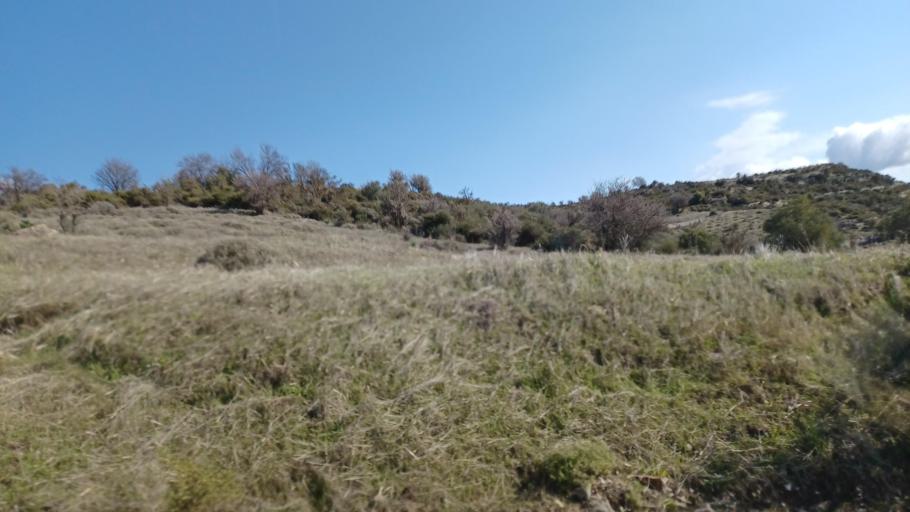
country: CY
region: Limassol
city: Pachna
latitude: 34.8211
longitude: 32.6891
